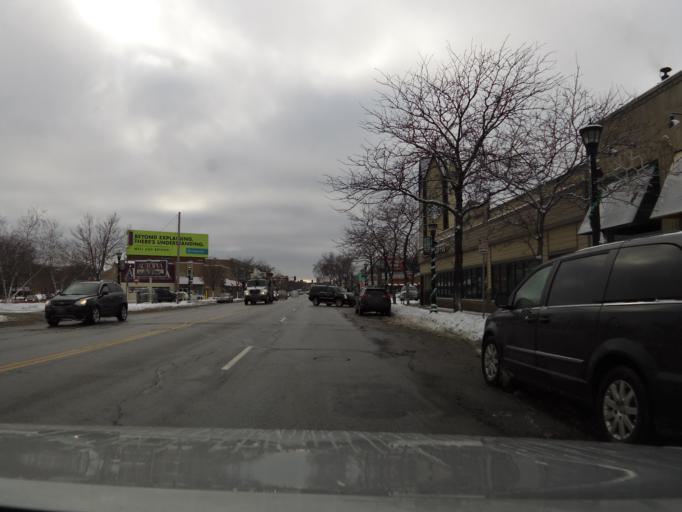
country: US
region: Minnesota
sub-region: Hennepin County
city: Minneapolis
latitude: 44.9606
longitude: -93.2930
